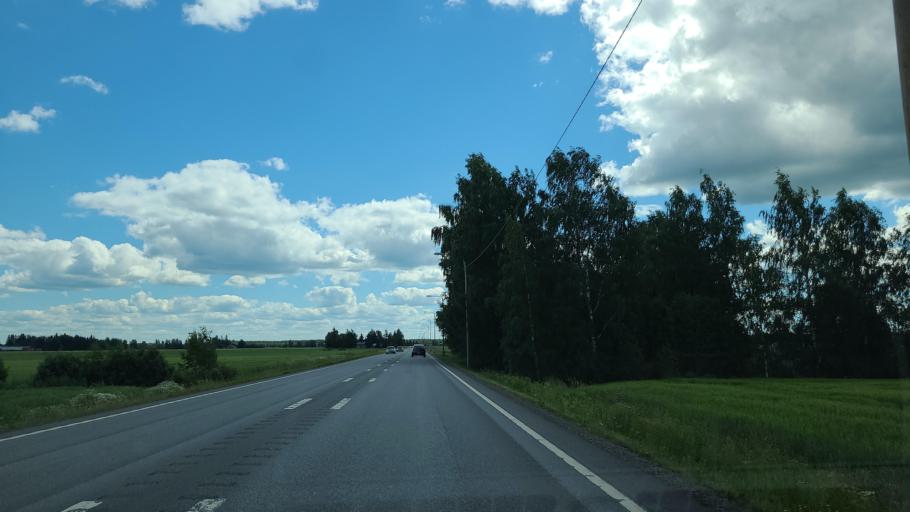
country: FI
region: Southern Ostrobothnia
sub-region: Seinaejoki
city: Ylistaro
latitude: 62.9407
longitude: 22.4653
